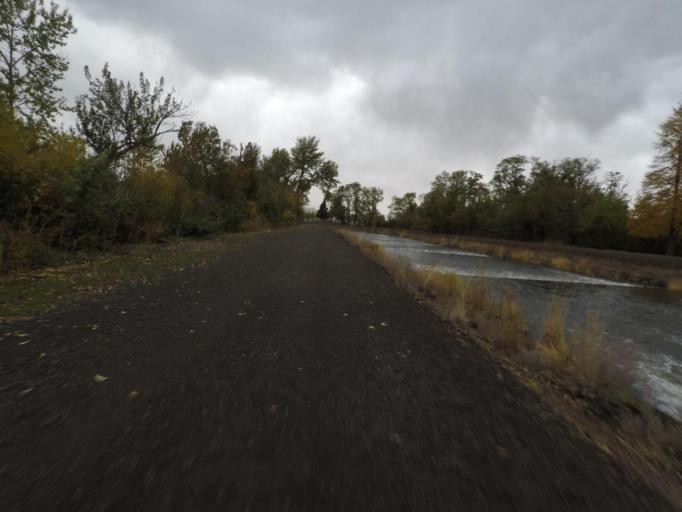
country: US
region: Washington
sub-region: Walla Walla County
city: Walla Walla East
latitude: 46.0763
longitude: -118.2765
